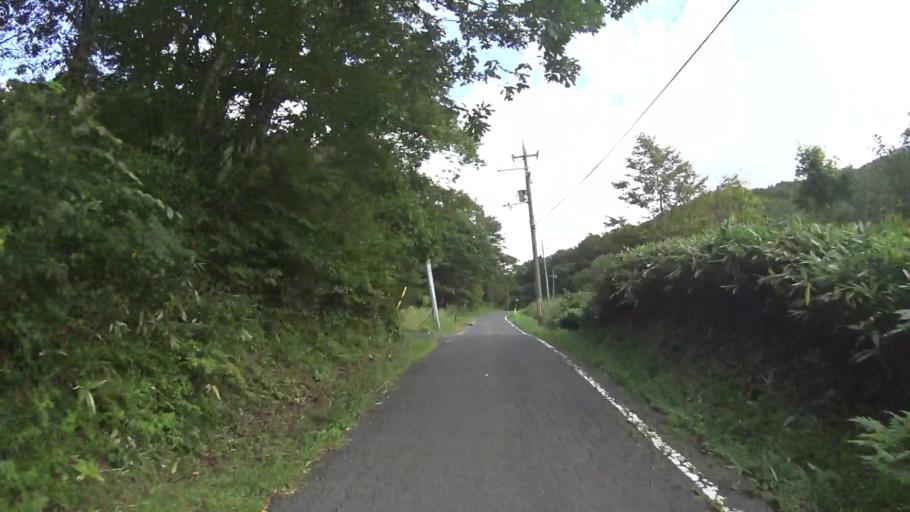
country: JP
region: Kyoto
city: Miyazu
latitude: 35.6508
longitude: 135.1805
